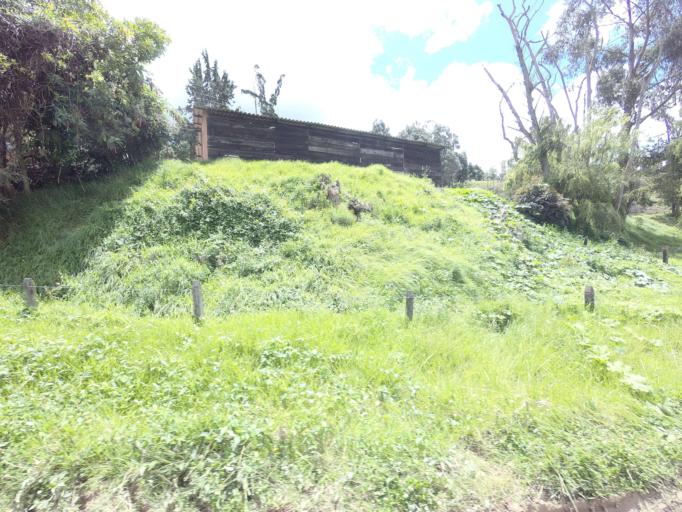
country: CO
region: Cundinamarca
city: Tabio
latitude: 4.9452
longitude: -74.0870
